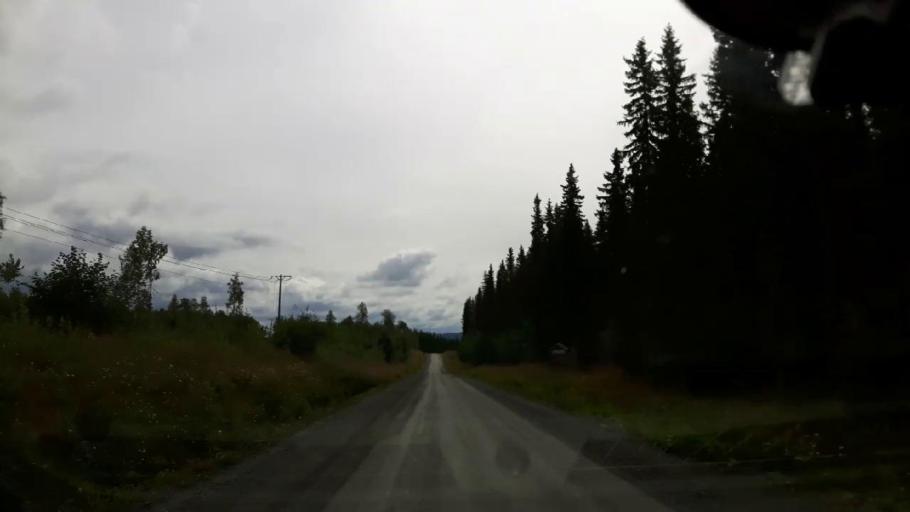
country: SE
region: Jaemtland
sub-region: Krokoms Kommun
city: Valla
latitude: 63.6486
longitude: 13.9871
